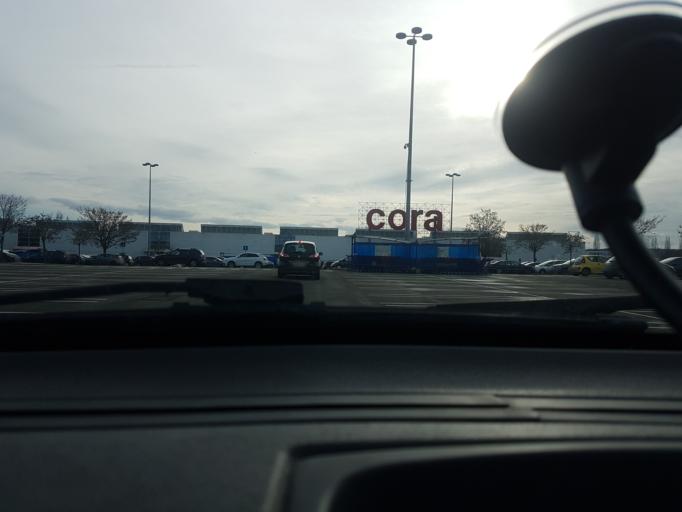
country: FR
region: Franche-Comte
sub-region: Territoire de Belfort
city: Andelnans
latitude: 47.5996
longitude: 6.8618
